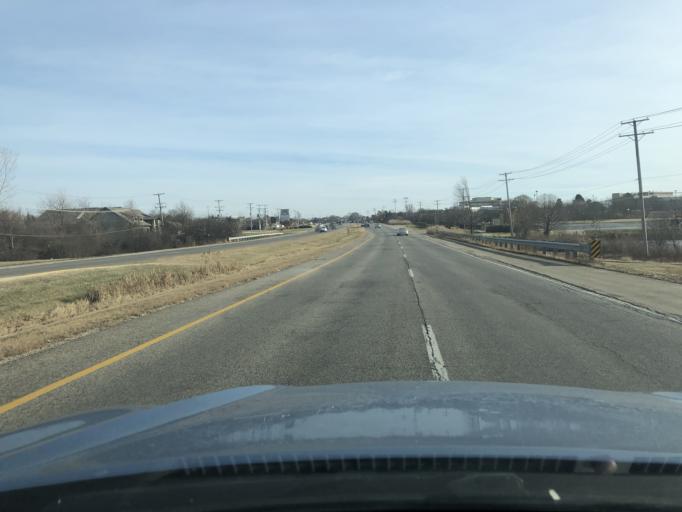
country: US
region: Illinois
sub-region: Cook County
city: South Barrington
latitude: 42.0586
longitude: -88.1414
